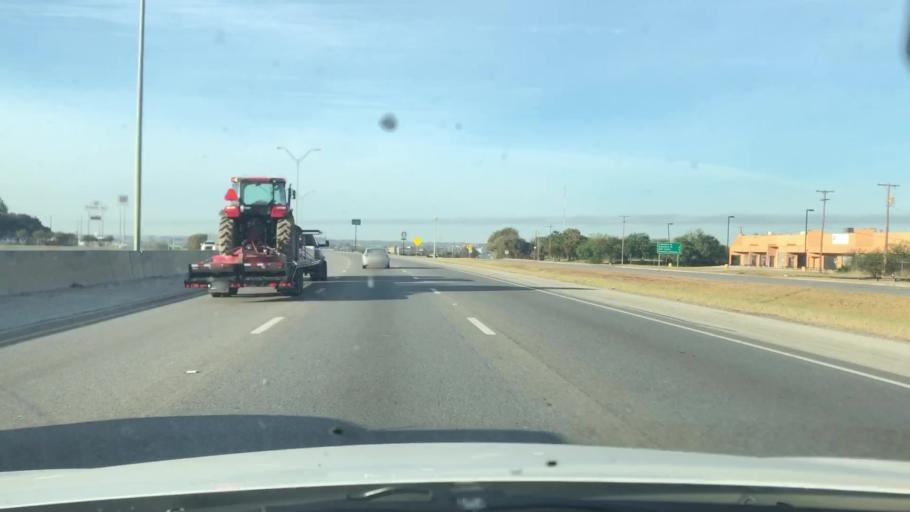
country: US
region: Texas
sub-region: Bexar County
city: Kirby
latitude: 29.4287
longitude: -98.4182
